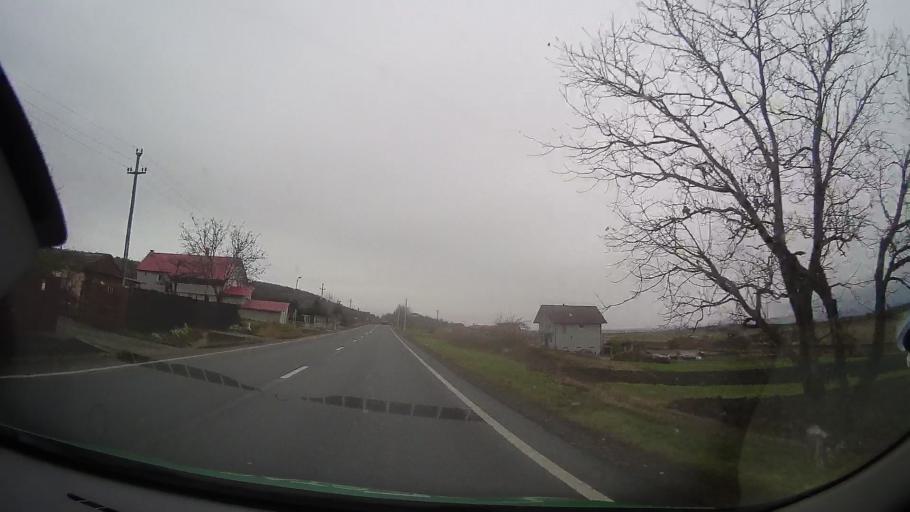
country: RO
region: Mures
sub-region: Comuna Breaza
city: Breaza
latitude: 46.7729
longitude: 24.6569
